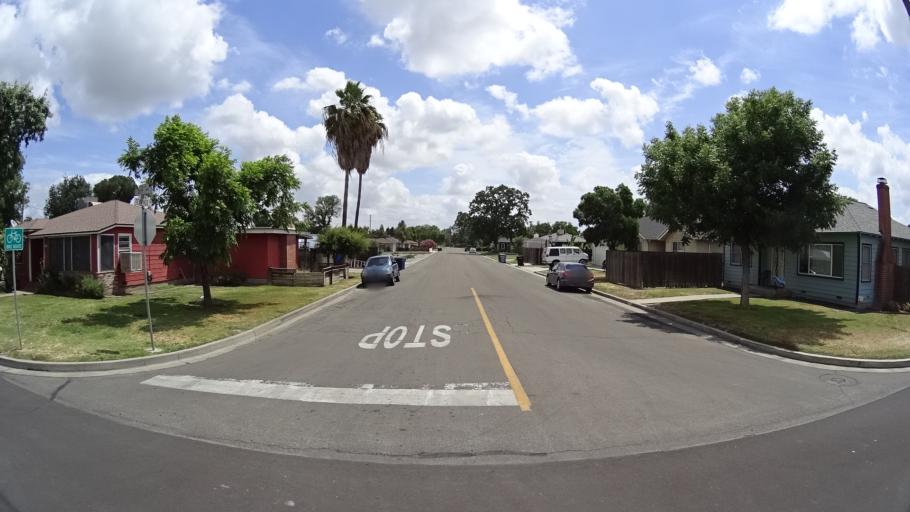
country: US
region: California
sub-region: Kings County
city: Hanford
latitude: 36.3462
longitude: -119.6551
